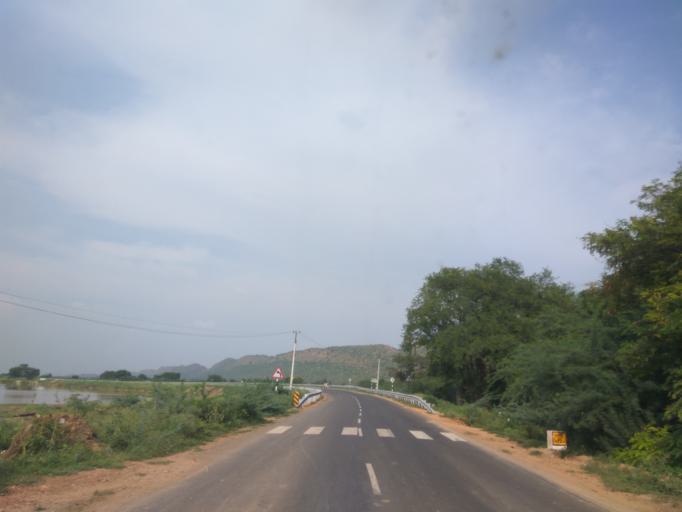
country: IN
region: Andhra Pradesh
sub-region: Prakasam
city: Markapur
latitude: 15.8214
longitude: 79.2706
